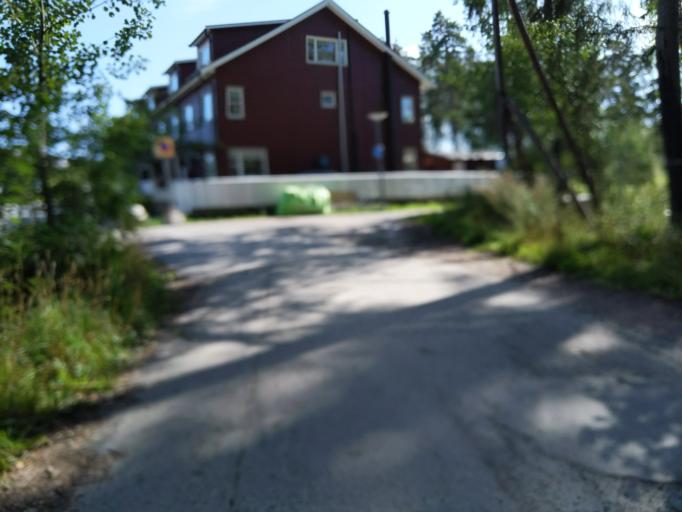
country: SE
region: Stockholm
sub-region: Solna Kommun
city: Rasunda
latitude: 59.3843
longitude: 17.9741
